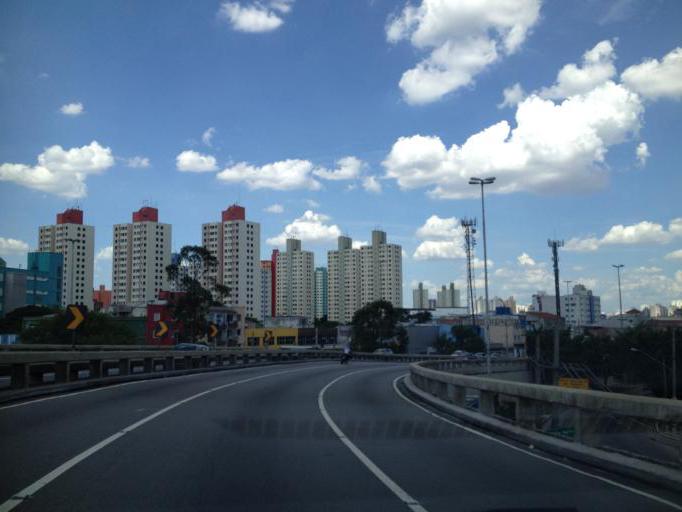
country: BR
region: Sao Paulo
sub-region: Sao Paulo
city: Sao Paulo
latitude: -23.5520
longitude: -46.6256
